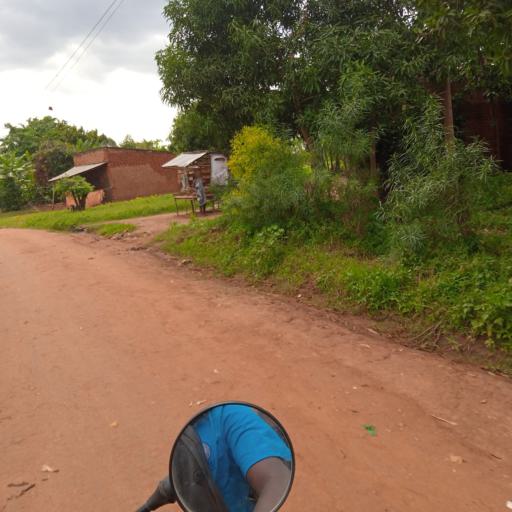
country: UG
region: Eastern Region
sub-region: Mbale District
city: Mbale
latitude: 1.1240
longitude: 34.1818
